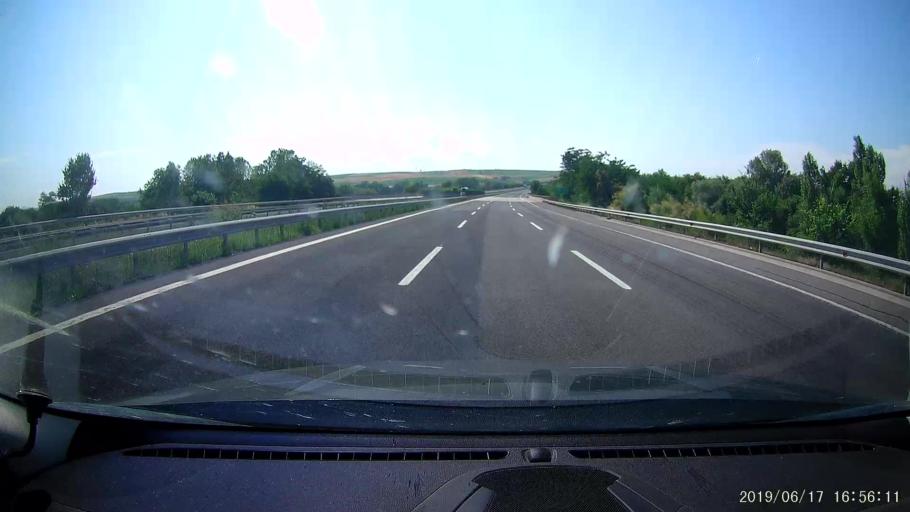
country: TR
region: Edirne
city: Haskoy
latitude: 41.5844
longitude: 26.9437
